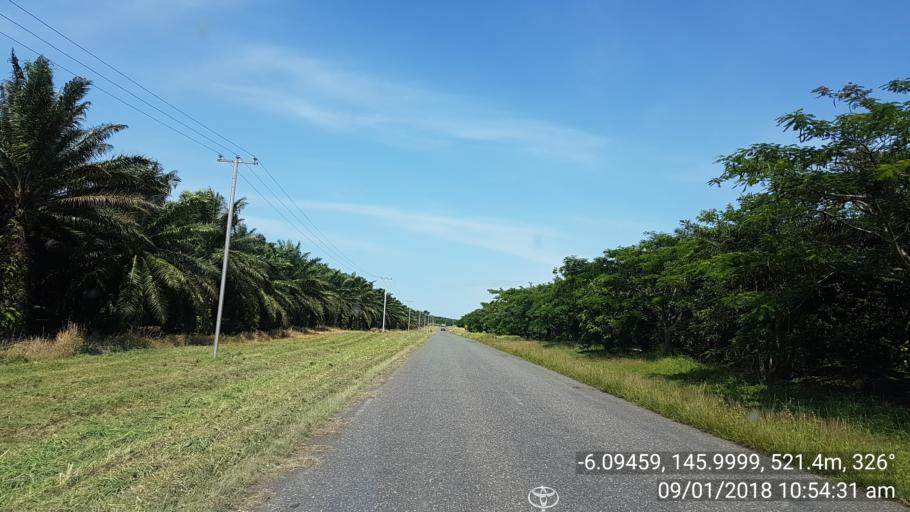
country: PG
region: Eastern Highlands
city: Kainantu
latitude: -6.0947
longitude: 146.0000
